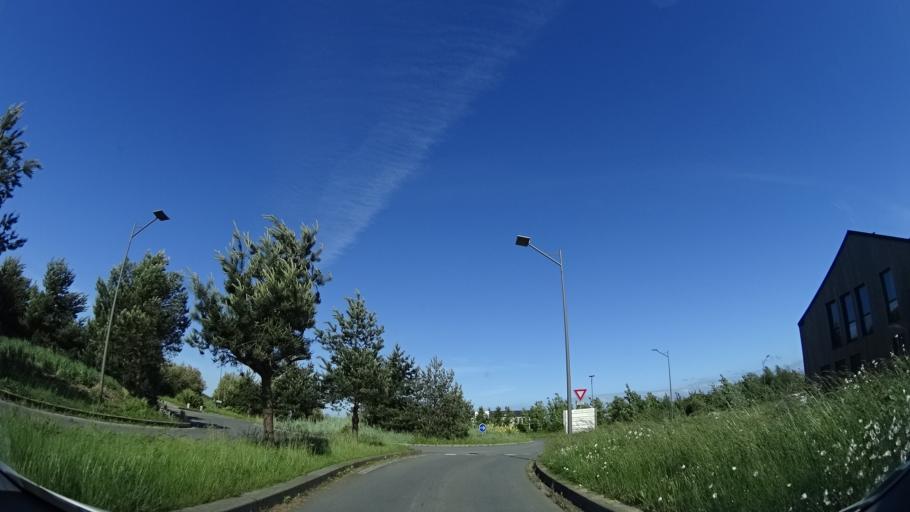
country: FR
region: Brittany
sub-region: Departement d'Ille-et-Vilaine
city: Saint-Jouan-des-Guerets
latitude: 48.6131
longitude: -1.9756
